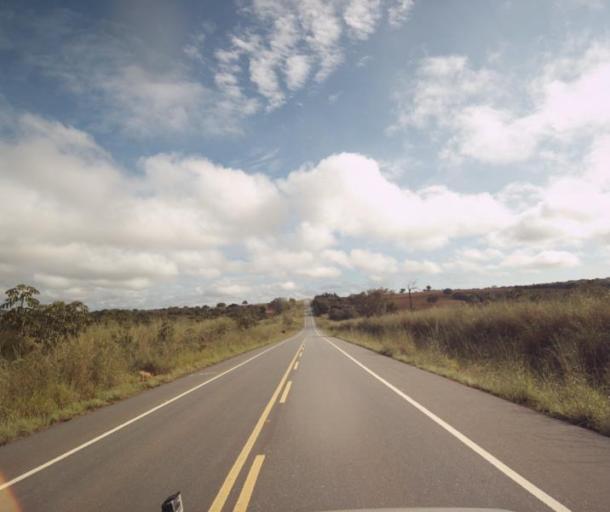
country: BR
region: Goias
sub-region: Barro Alto
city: Barro Alto
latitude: -15.2650
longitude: -48.6864
